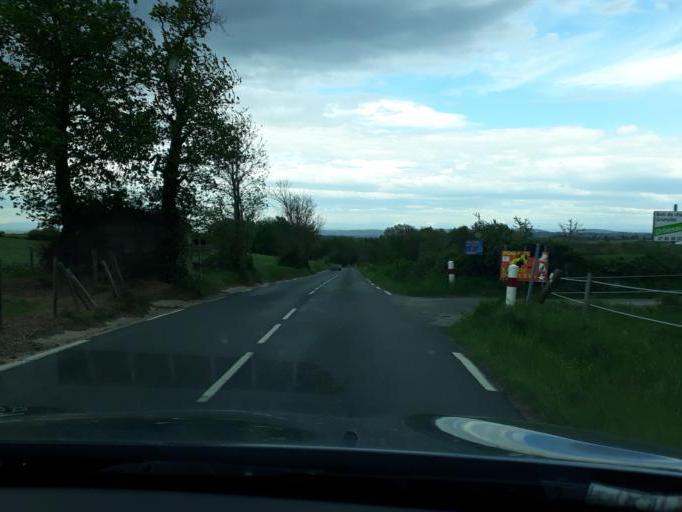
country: FR
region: Rhone-Alpes
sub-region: Departement du Rhone
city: Soucieu-en-Jarrest
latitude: 45.6781
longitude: 4.7188
